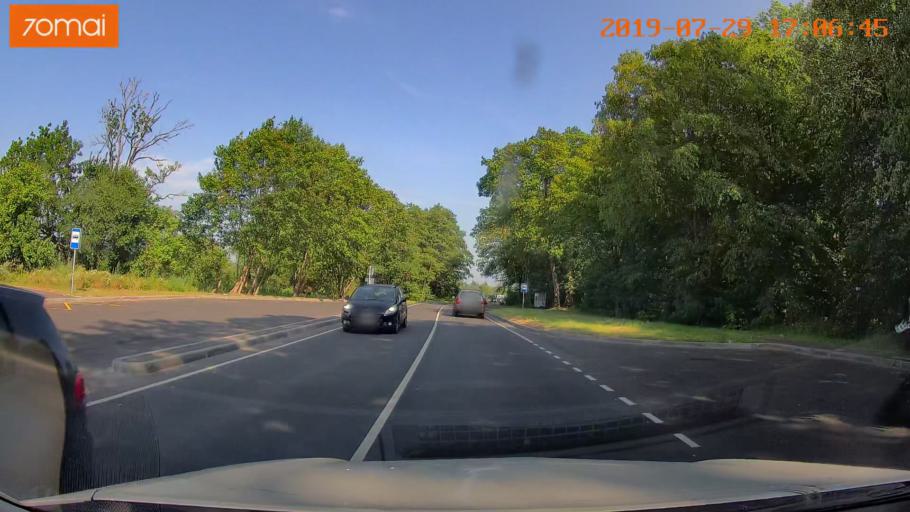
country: RU
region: Kaliningrad
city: Vzmorye
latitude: 54.8192
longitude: 20.3124
